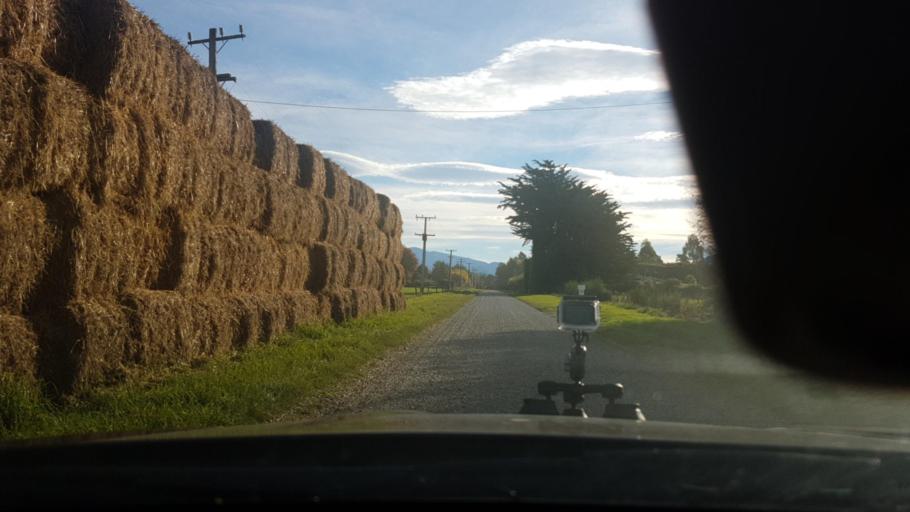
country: NZ
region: Canterbury
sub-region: Waimakariri District
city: Oxford
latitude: -43.2867
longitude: 172.1522
